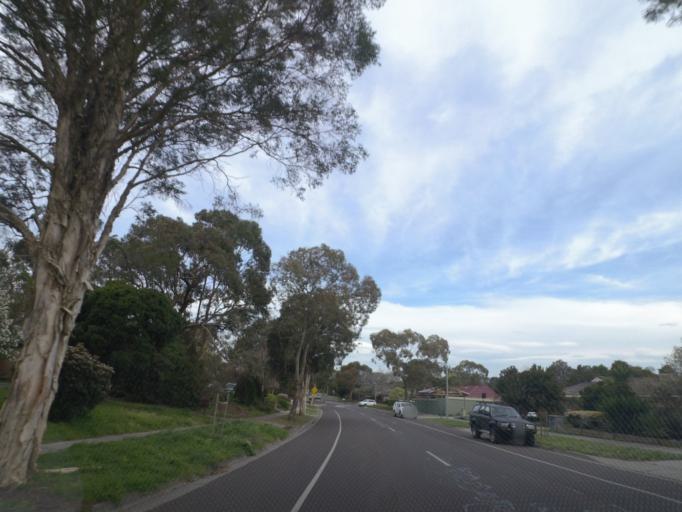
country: AU
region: Victoria
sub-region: Knox
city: Knoxfield
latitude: -37.8917
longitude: 145.2654
